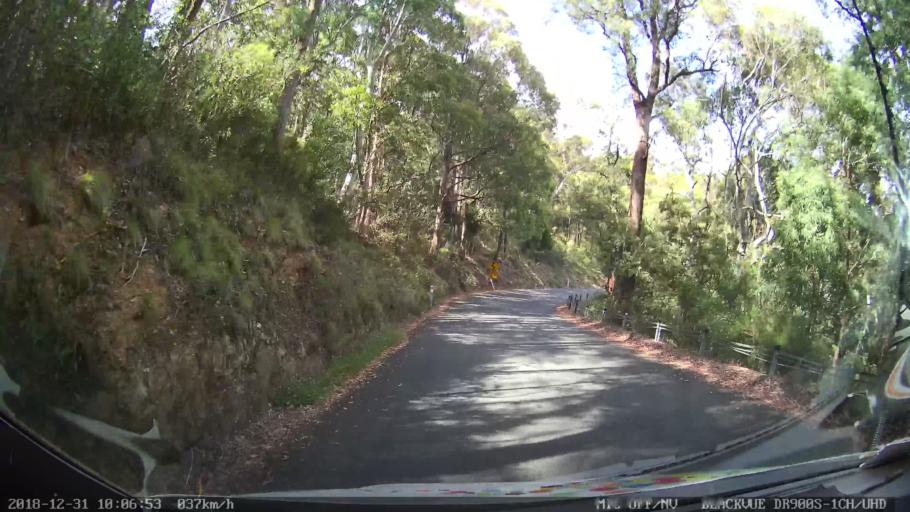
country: AU
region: New South Wales
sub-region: Snowy River
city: Jindabyne
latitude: -36.5309
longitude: 148.1869
